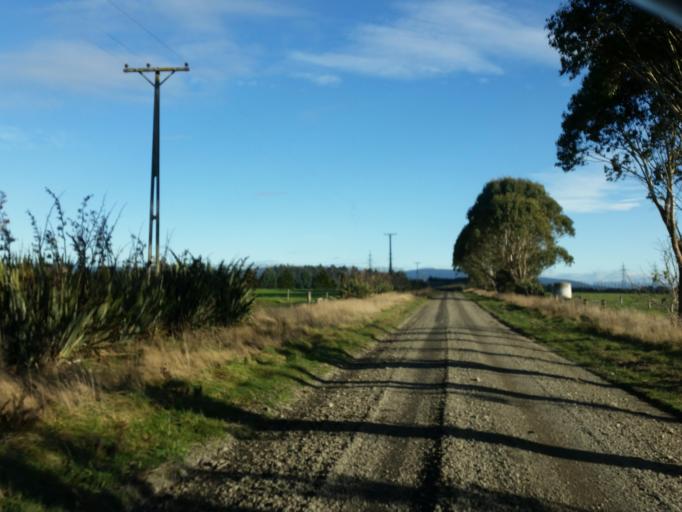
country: NZ
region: Southland
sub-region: Southland District
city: Winton
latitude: -46.1395
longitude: 168.1376
